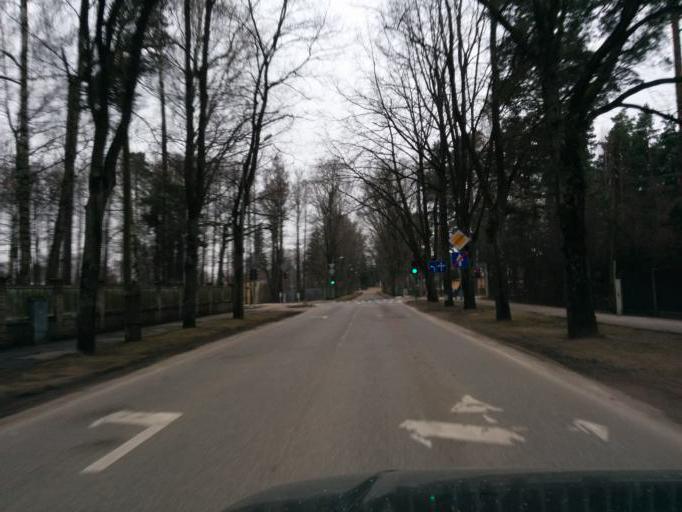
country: LV
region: Babite
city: Pinki
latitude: 56.9764
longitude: 23.8539
